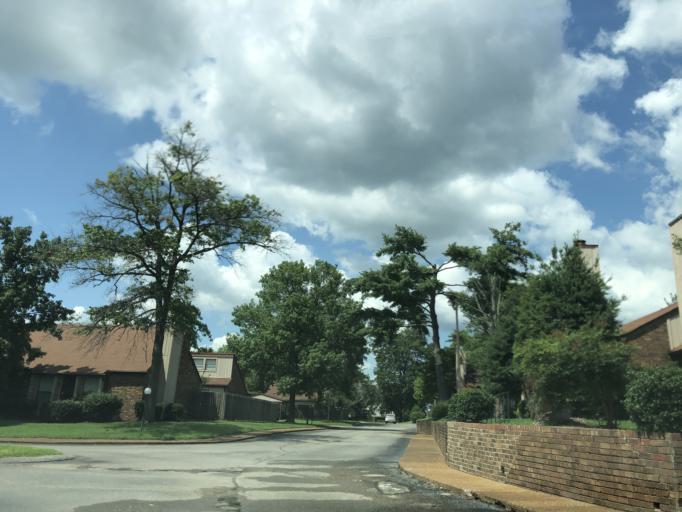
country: US
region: Tennessee
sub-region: Davidson County
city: Lakewood
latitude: 36.2236
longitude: -86.5959
